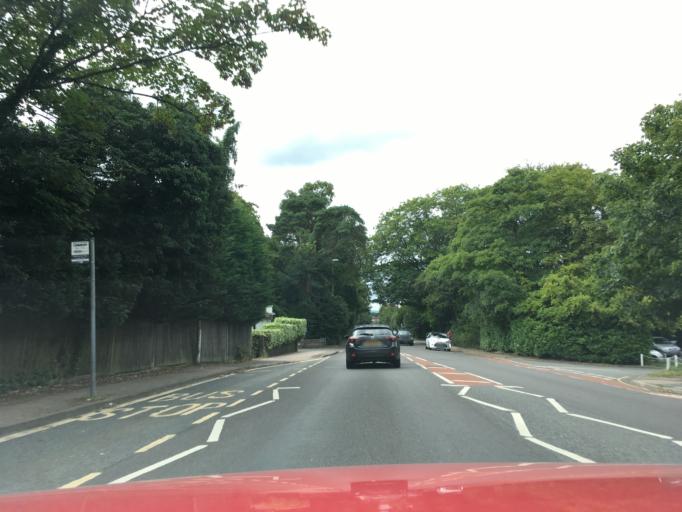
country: GB
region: England
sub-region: Surrey
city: Felbridge
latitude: 51.1338
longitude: -0.0247
